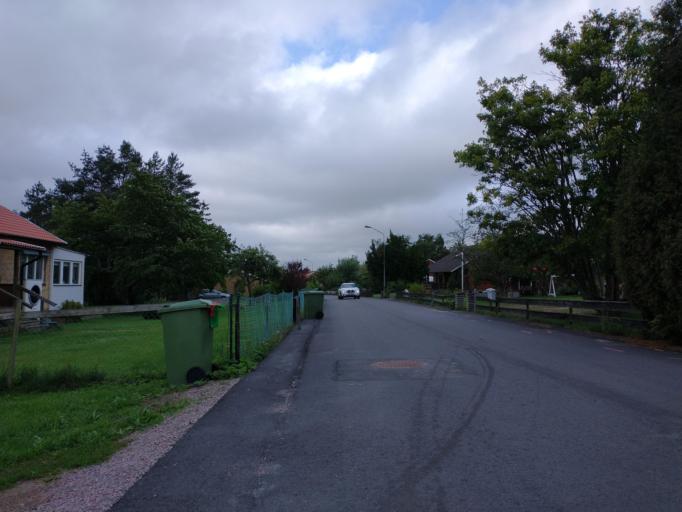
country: SE
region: Kalmar
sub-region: Kalmar Kommun
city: Lindsdal
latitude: 56.7816
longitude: 16.2938
